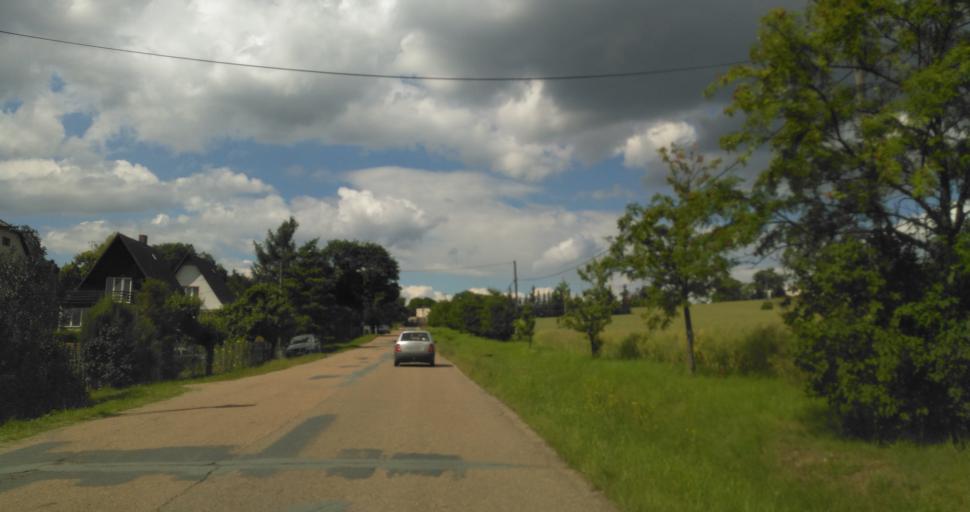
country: CZ
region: Plzensky
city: Zbiroh
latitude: 49.8531
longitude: 13.7525
